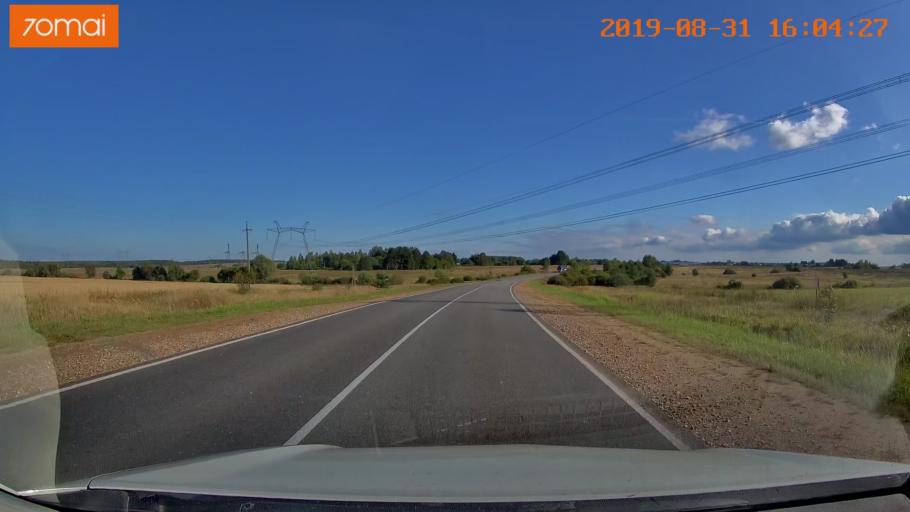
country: RU
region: Kaluga
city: Yukhnov
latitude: 54.6542
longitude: 35.3297
